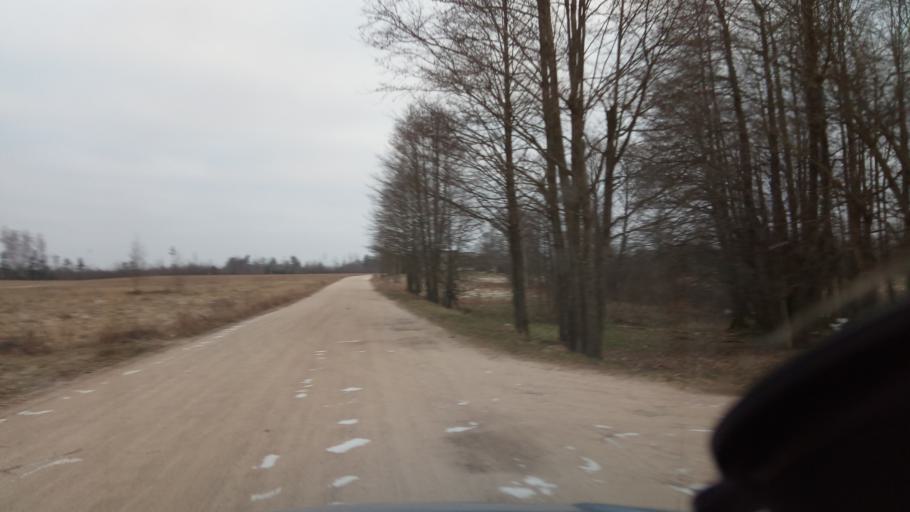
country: LT
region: Alytaus apskritis
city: Varena
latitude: 54.3624
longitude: 24.5456
